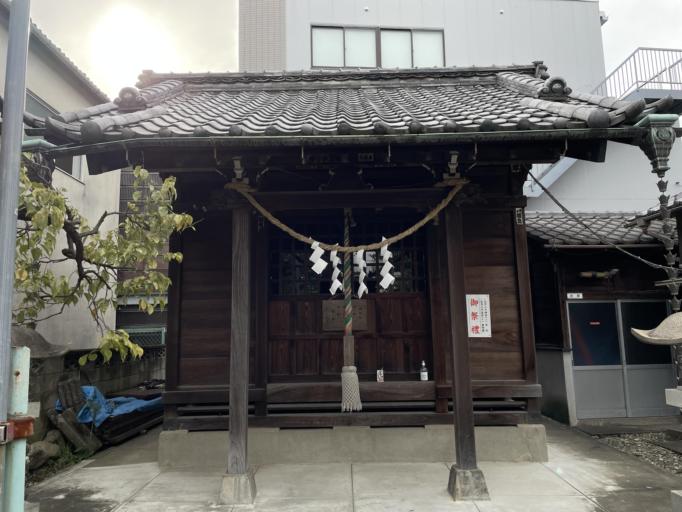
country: JP
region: Saitama
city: Soka
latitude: 35.7841
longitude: 139.7738
